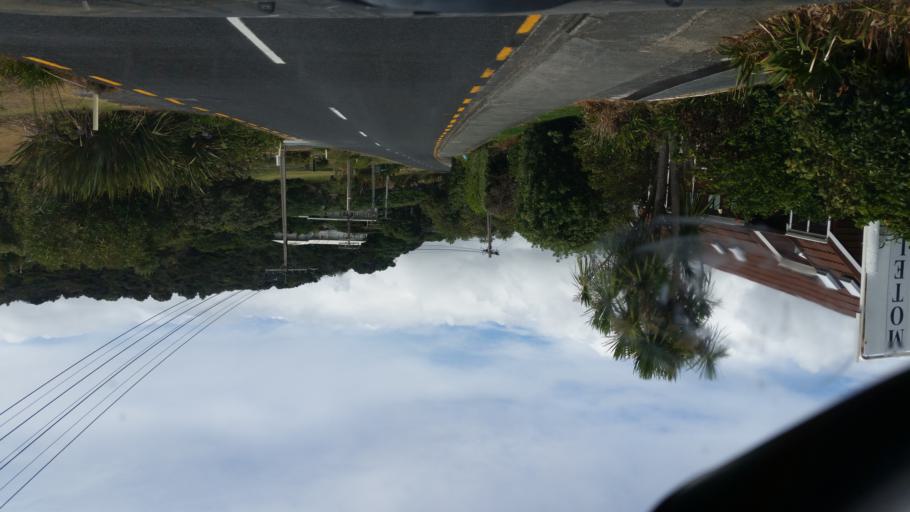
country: NZ
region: Auckland
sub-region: Auckland
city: Wellsford
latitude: -36.0810
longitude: 174.5949
